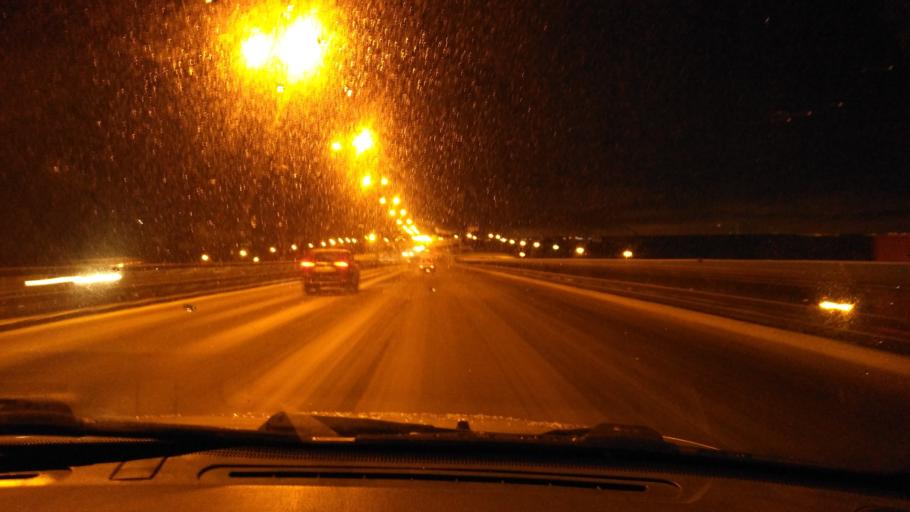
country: RU
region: St.-Petersburg
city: Kronshtadt
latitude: 60.0265
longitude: 29.8405
